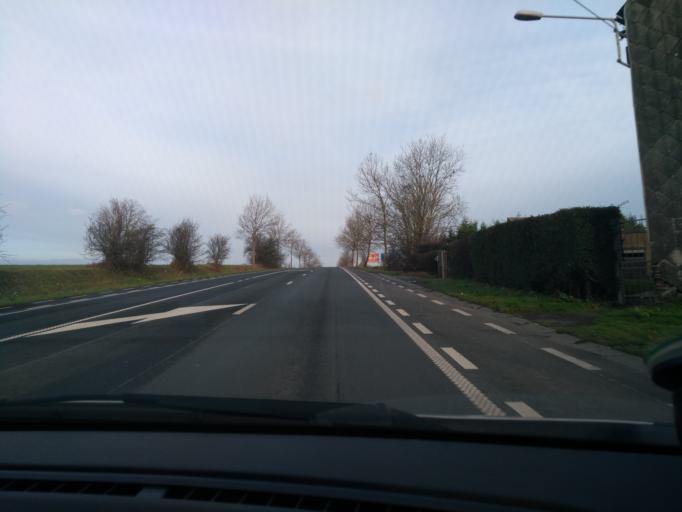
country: BE
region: Wallonia
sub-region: Province du Hainaut
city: Quevy-le-Petit
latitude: 50.3821
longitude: 3.9660
